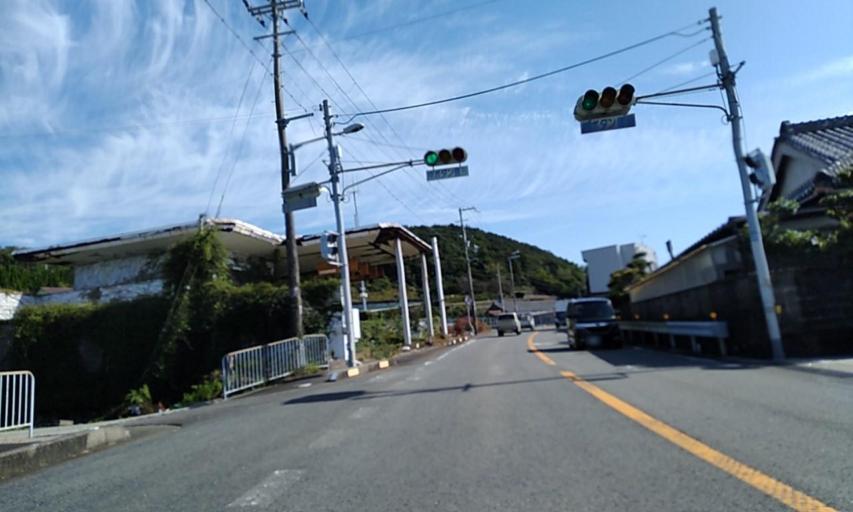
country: JP
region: Wakayama
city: Gobo
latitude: 33.8369
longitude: 135.1775
